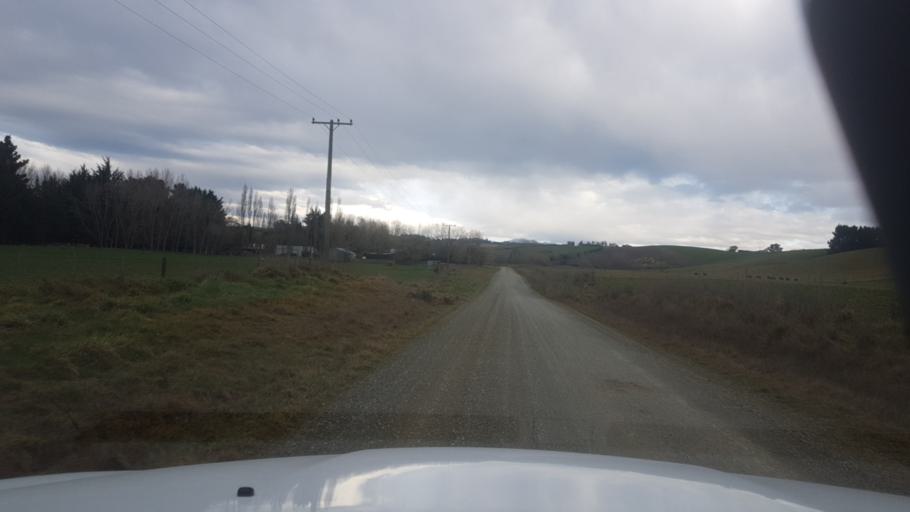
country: NZ
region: Canterbury
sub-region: Timaru District
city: Pleasant Point
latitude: -44.3391
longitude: 171.1743
